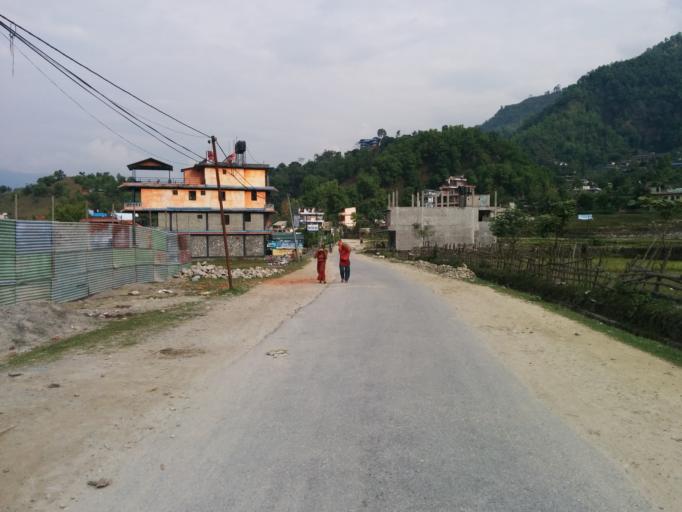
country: NP
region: Western Region
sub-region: Gandaki Zone
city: Pokhara
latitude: 28.2236
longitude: 83.9525
